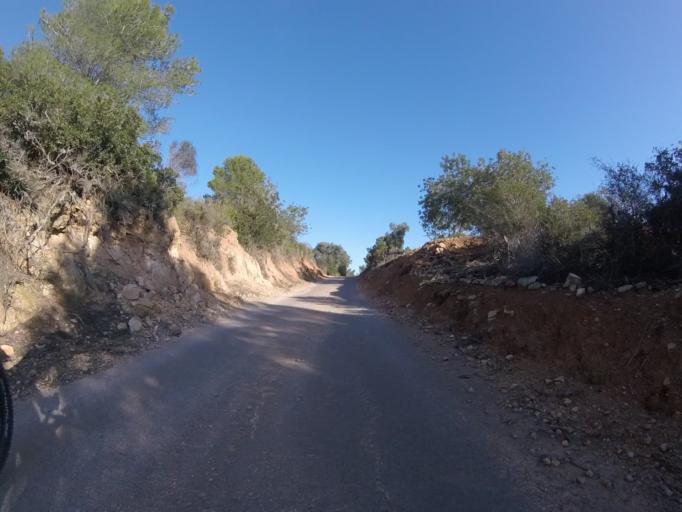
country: ES
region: Valencia
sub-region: Provincia de Castello
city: Alcala de Xivert
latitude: 40.2731
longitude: 0.2067
